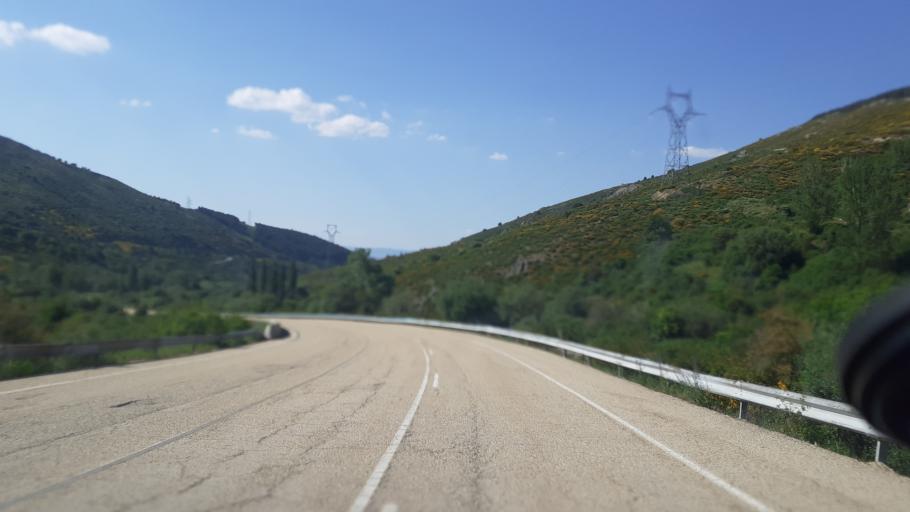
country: ES
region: Madrid
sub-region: Provincia de Madrid
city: Somosierra
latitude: 41.1448
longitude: -3.5781
